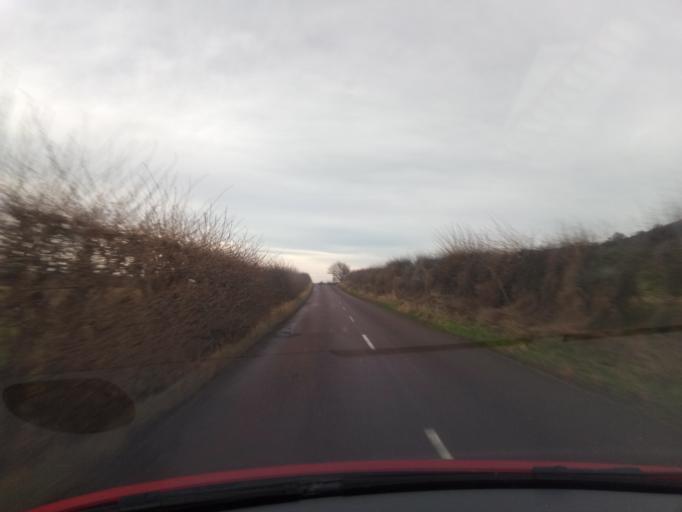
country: GB
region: England
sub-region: Northumberland
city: Kirknewton
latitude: 55.5628
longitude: -2.0826
